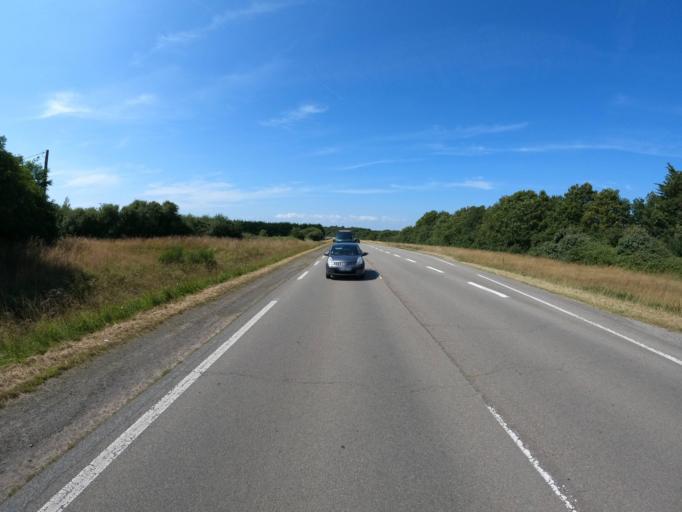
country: FR
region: Pays de la Loire
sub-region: Departement de la Loire-Atlantique
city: La Bernerie-en-Retz
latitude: 47.0970
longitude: -2.0368
